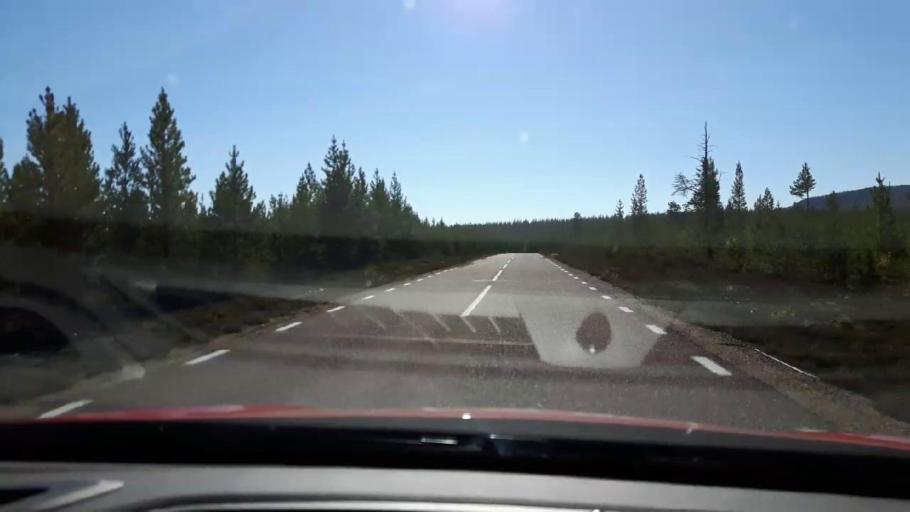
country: SE
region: Jaemtland
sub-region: Harjedalens Kommun
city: Sveg
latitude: 61.7148
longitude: 14.1686
